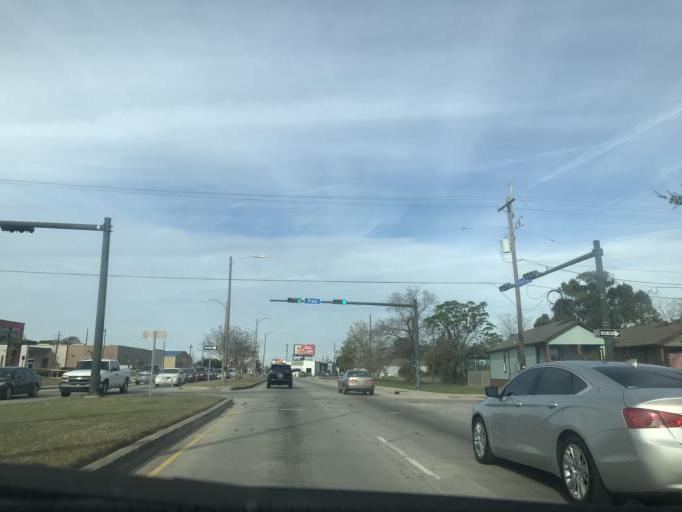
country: US
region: Louisiana
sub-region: Orleans Parish
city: New Orleans
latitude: 29.9588
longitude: -90.1106
